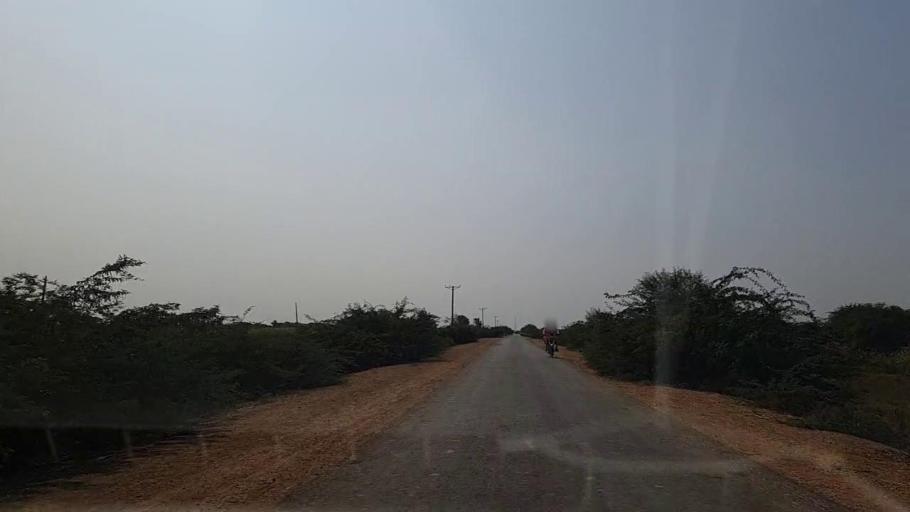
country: PK
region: Sindh
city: Chuhar Jamali
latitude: 24.3037
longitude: 67.9349
